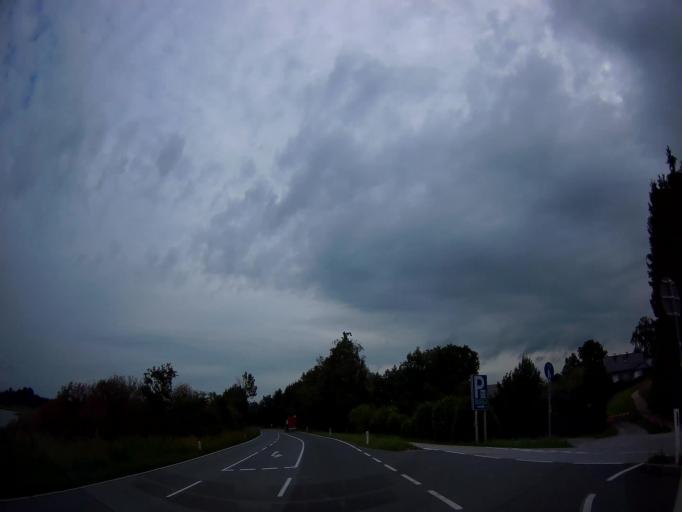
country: AT
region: Salzburg
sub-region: Politischer Bezirk Salzburg-Umgebung
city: Mattsee
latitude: 47.9763
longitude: 13.1043
